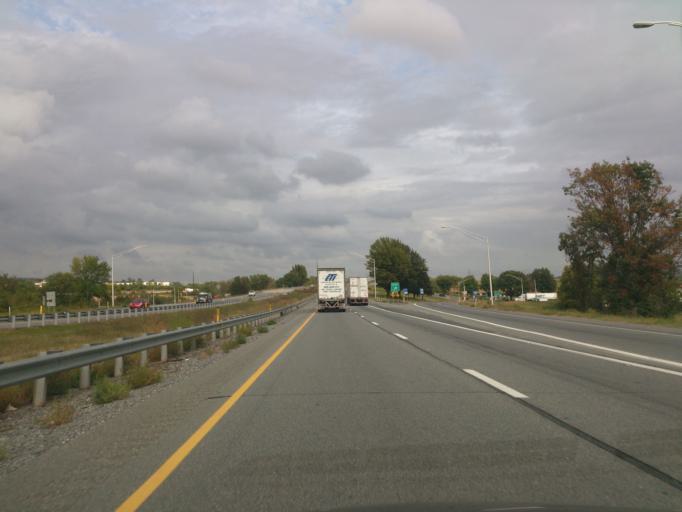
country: US
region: Pennsylvania
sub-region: Lancaster County
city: Swartzville
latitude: 40.2151
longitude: -76.0939
